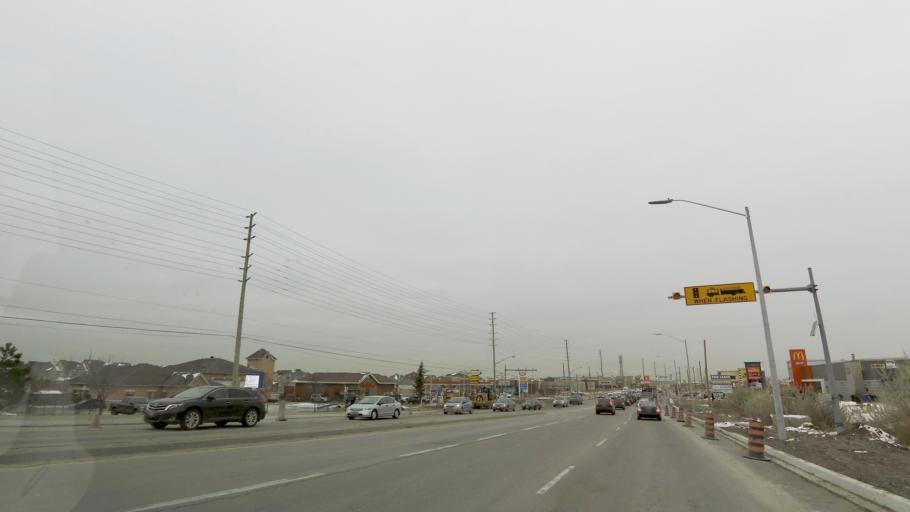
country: CA
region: Ontario
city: Vaughan
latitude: 43.8462
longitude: -79.5518
